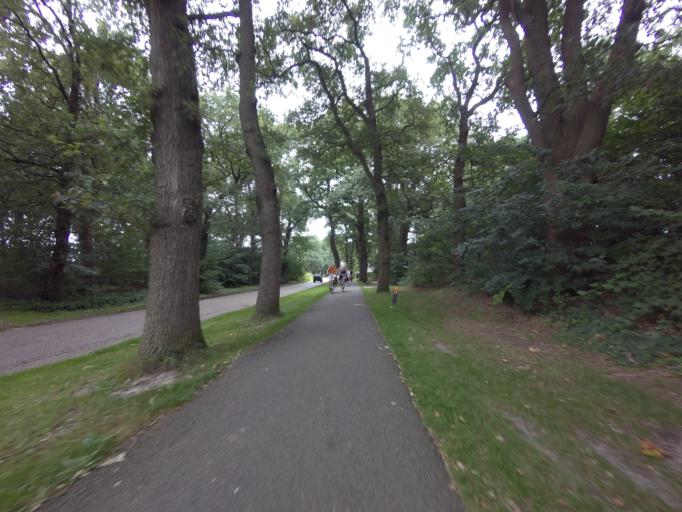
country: NL
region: Drenthe
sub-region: Gemeente Westerveld
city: Dwingeloo
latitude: 52.8590
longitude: 6.3210
